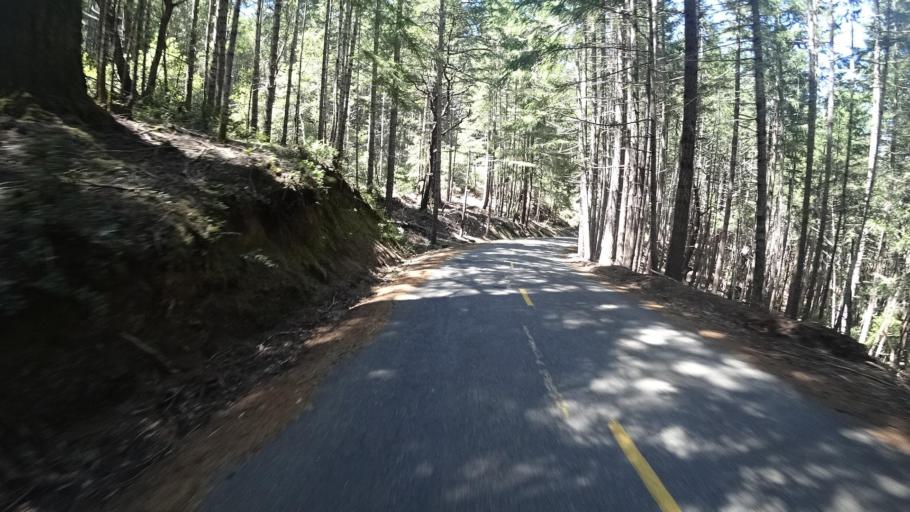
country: US
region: California
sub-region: Humboldt County
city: Rio Dell
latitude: 40.3084
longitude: -124.0625
